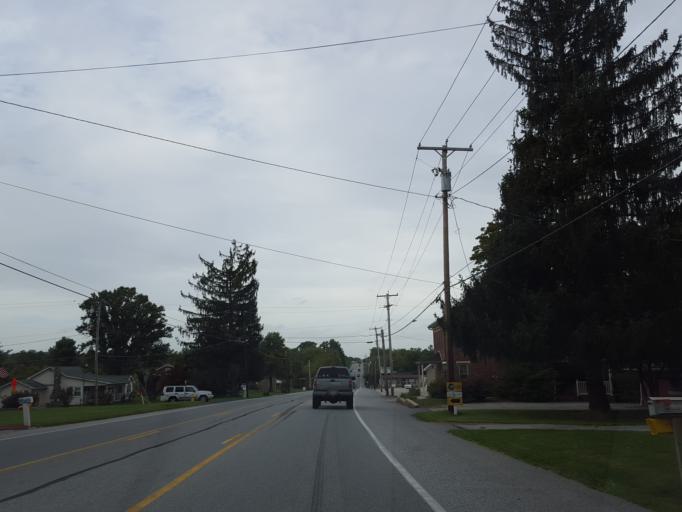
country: US
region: Pennsylvania
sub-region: Adams County
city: Abbottstown
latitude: 39.8936
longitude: -76.9600
